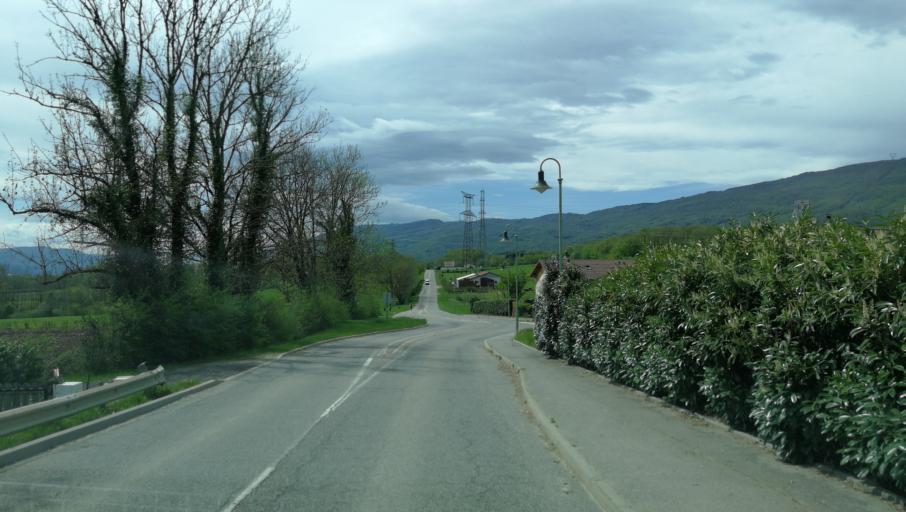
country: FR
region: Rhone-Alpes
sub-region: Departement de l'Ain
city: Bellegarde-sur-Valserine
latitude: 46.0731
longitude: 5.7832
